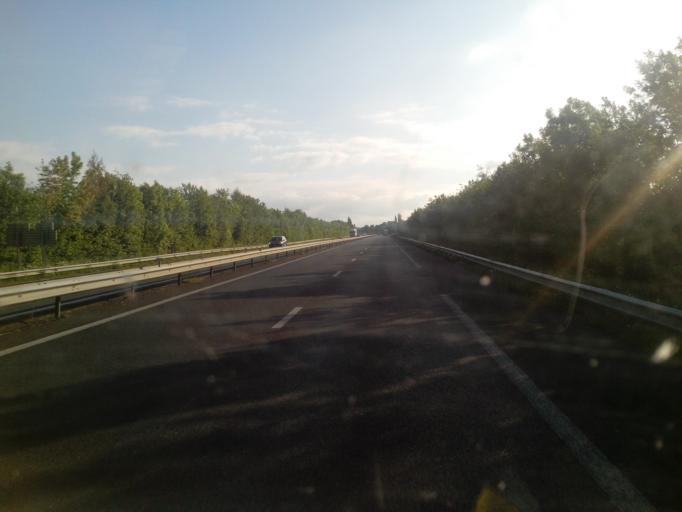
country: FR
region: Lower Normandy
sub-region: Departement du Calvados
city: Grainville-sur-Odon
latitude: 49.1150
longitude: -0.5867
